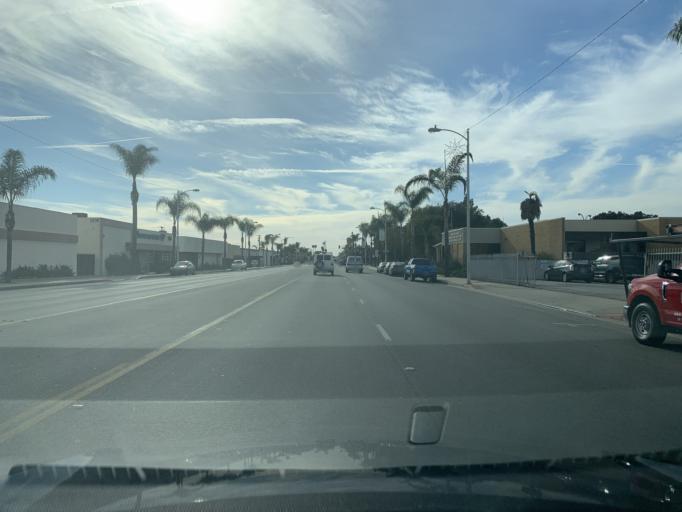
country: US
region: California
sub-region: Los Angeles County
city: South El Monte
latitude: 34.0453
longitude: -118.0448
